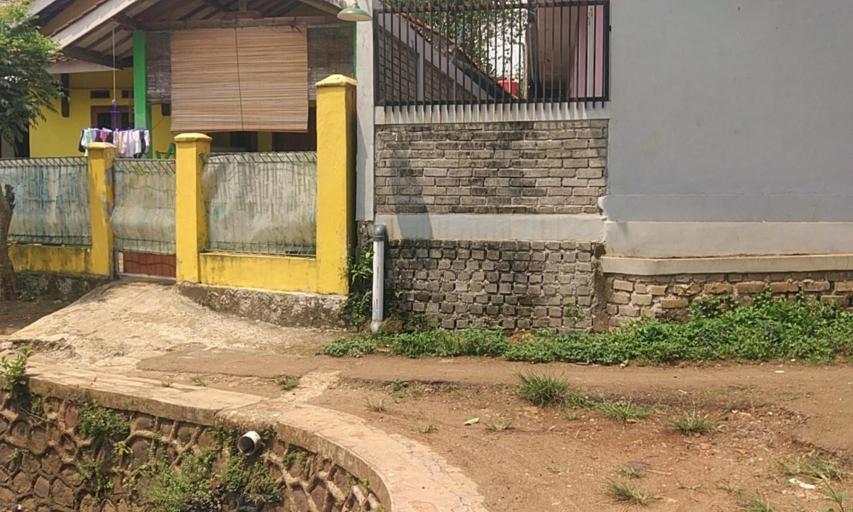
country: ID
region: West Java
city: Ciampea
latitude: -6.5304
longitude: 106.7275
